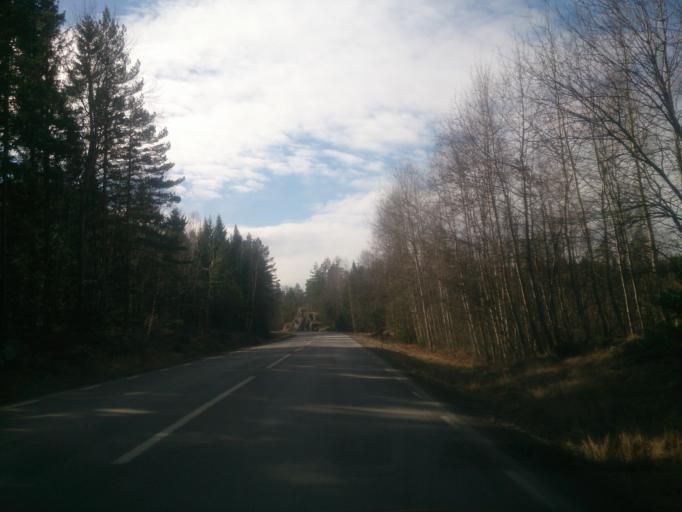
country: SE
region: OEstergoetland
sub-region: Finspangs Kommun
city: Finspang
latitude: 58.6207
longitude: 15.8156
